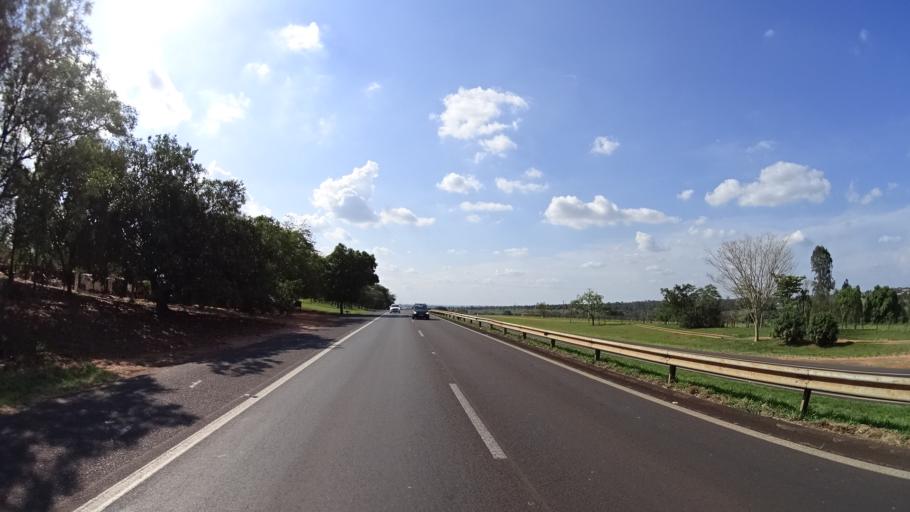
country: BR
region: Sao Paulo
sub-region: Sao Jose Do Rio Preto
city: Sao Jose do Rio Preto
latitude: -20.9198
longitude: -49.2825
